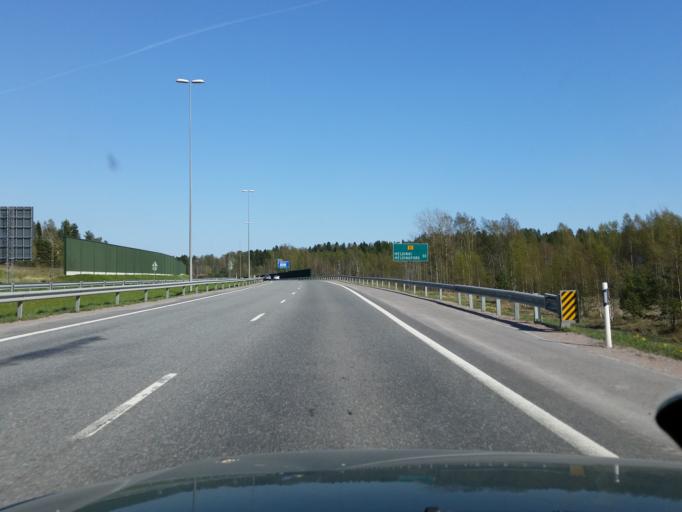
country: FI
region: Uusimaa
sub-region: Helsinki
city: Kirkkonummi
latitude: 60.1159
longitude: 24.4576
